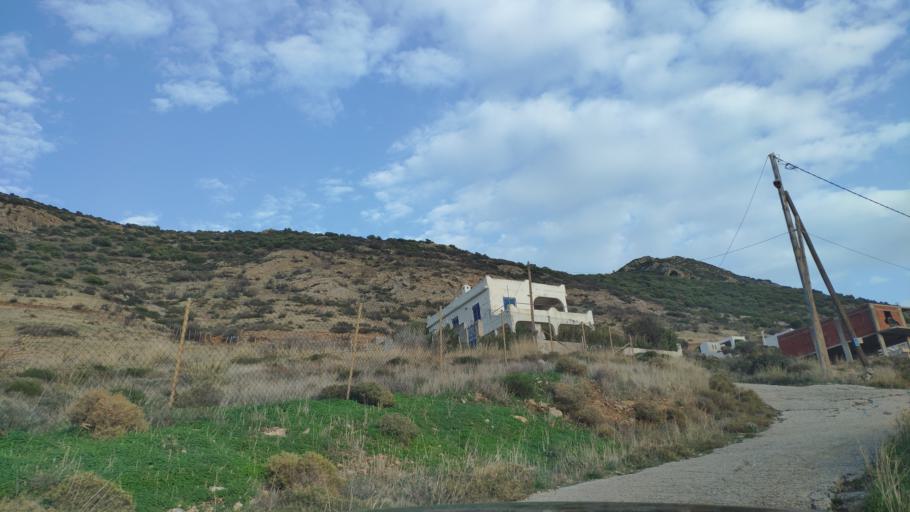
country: GR
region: Attica
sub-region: Nomarchia Anatolikis Attikis
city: Limin Mesoyaias
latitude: 37.9052
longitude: 24.0242
